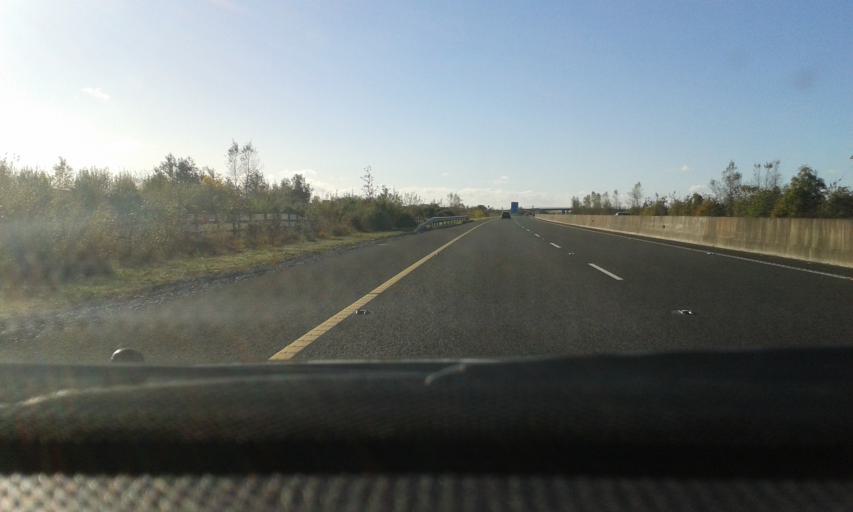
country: IE
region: Munster
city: Thurles
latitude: 52.6768
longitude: -7.6843
